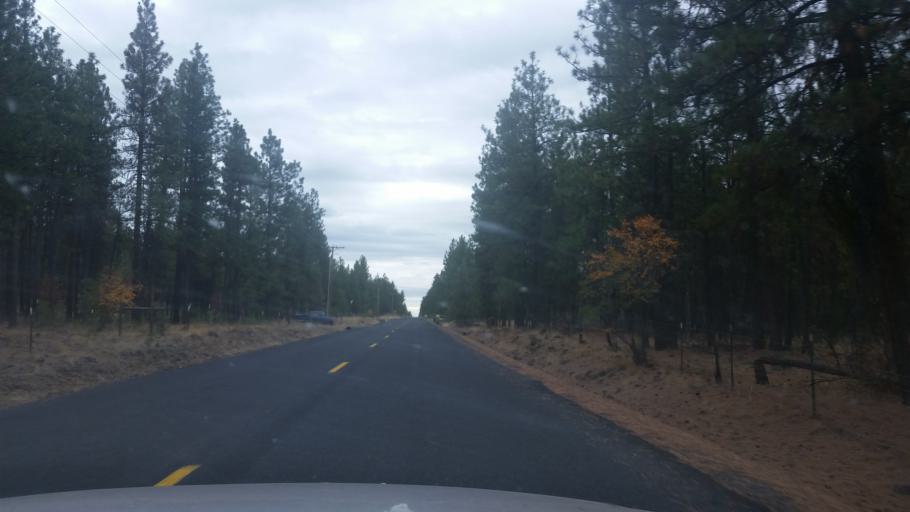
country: US
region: Washington
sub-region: Spokane County
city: Medical Lake
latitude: 47.4780
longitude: -117.7792
